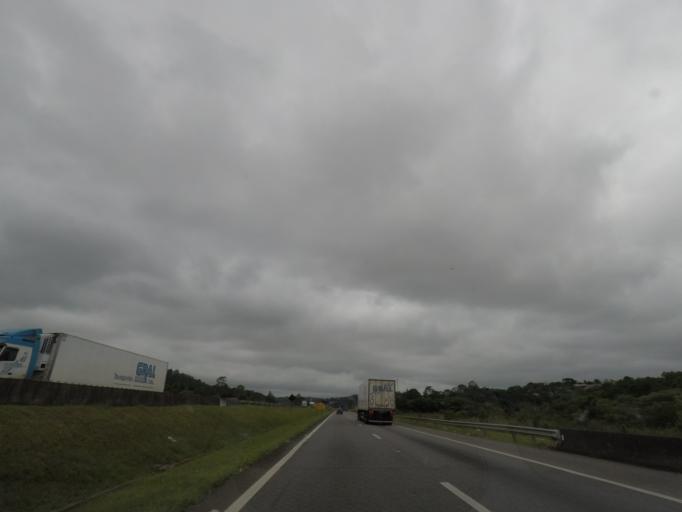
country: BR
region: Sao Paulo
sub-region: Bom Jesus Dos Perdoes
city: Bom Jesus dos Perdoes
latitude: -23.1702
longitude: -46.4386
